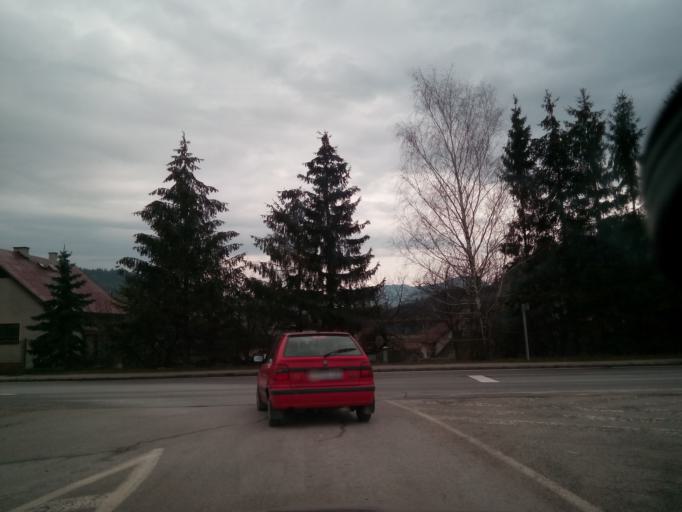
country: SK
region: Zilinsky
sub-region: Okres Dolny Kubin
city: Dolny Kubin
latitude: 49.1931
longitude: 19.1944
